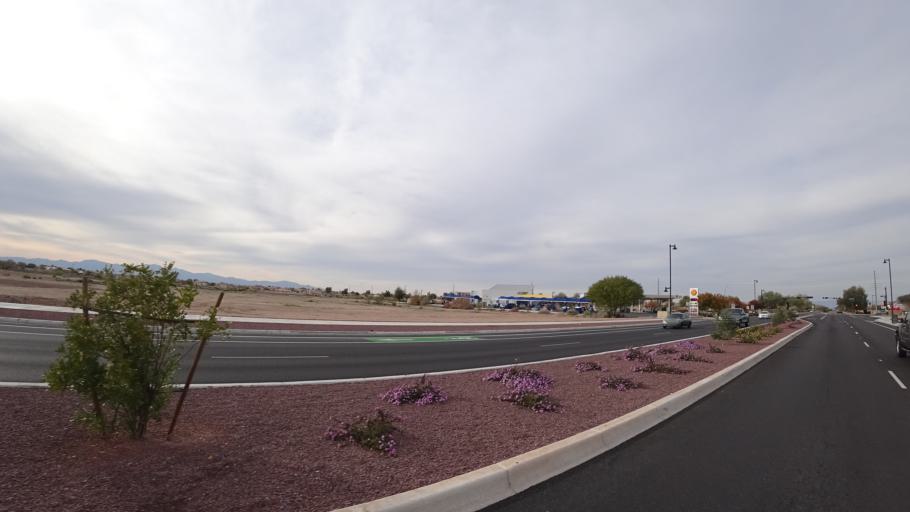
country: US
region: Arizona
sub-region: Maricopa County
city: El Mirage
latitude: 33.5927
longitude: -112.3246
